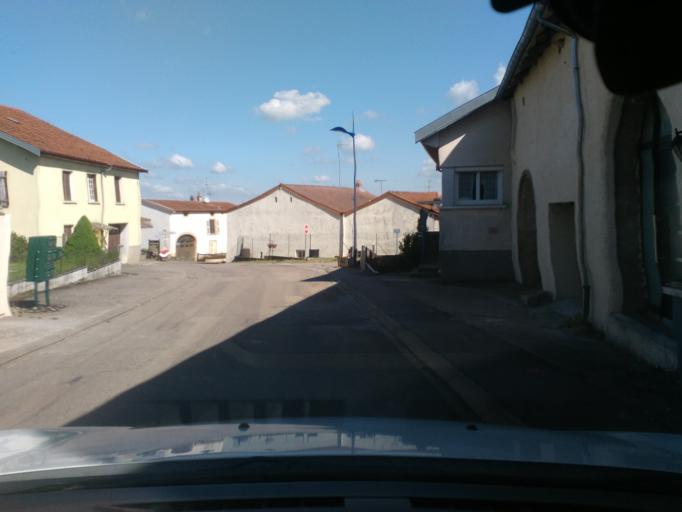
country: FR
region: Lorraine
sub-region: Departement des Vosges
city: Mirecourt
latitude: 48.3221
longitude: 6.1476
